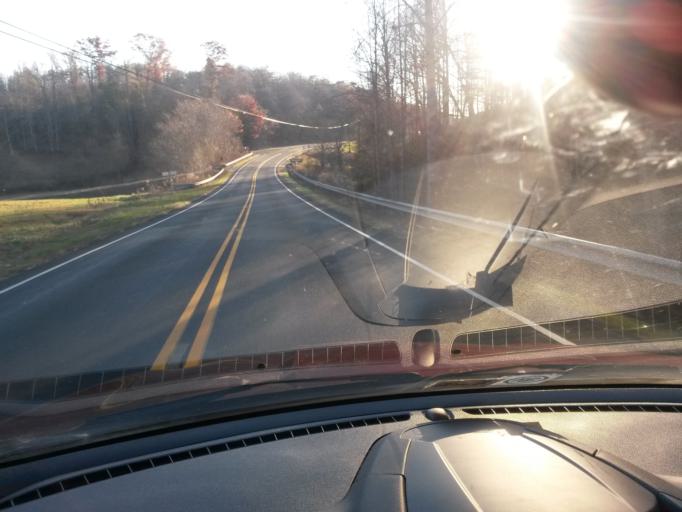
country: US
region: Virginia
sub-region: Amherst County
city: Amherst
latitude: 37.6662
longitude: -79.1664
